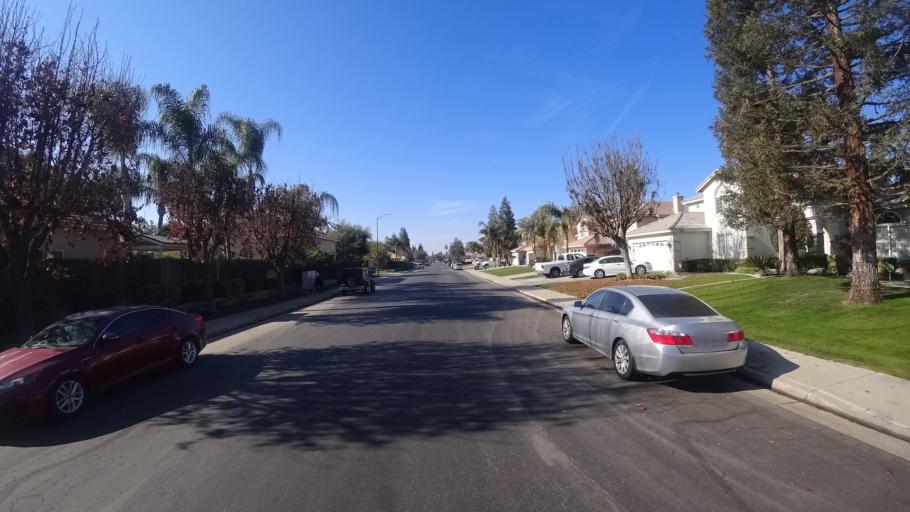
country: US
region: California
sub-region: Kern County
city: Greenacres
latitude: 35.3189
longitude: -119.1196
